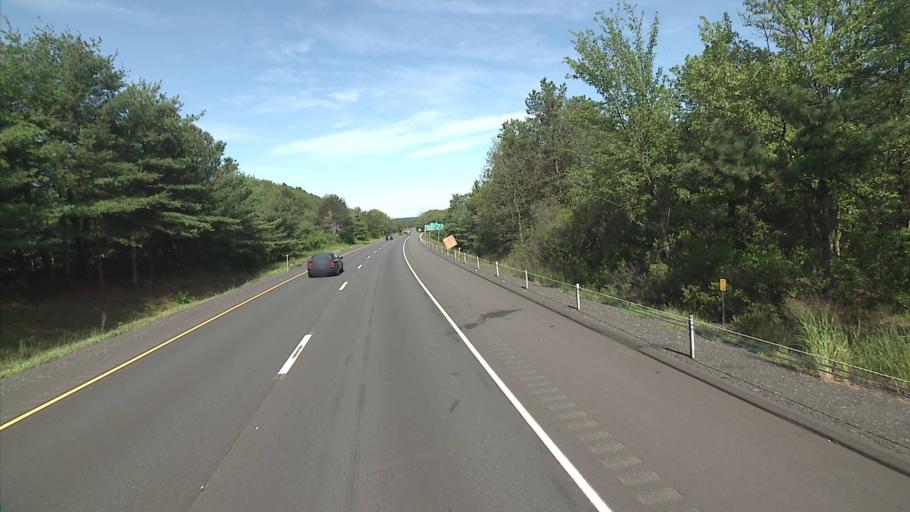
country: US
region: Connecticut
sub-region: Hartford County
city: Terramuggus
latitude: 41.6600
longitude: -72.5166
